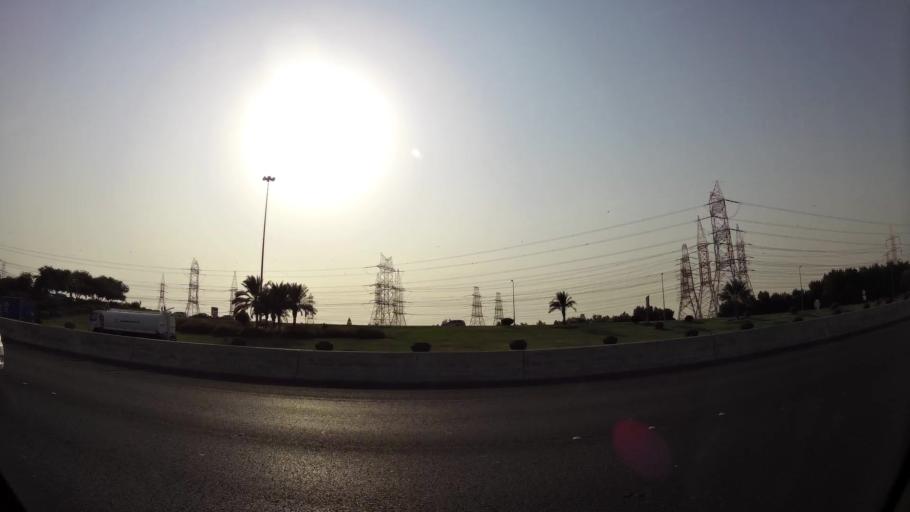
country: KW
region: Mubarak al Kabir
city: Sabah as Salim
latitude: 29.2403
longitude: 48.0498
